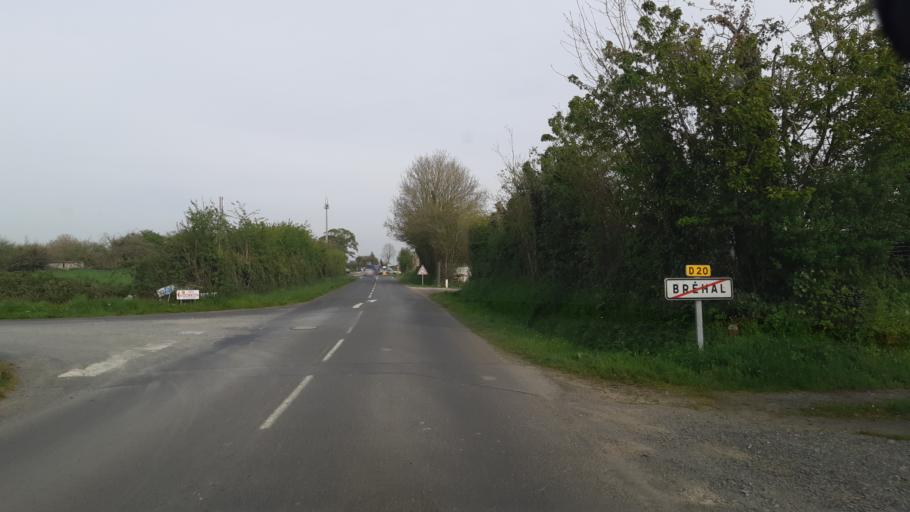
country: FR
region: Lower Normandy
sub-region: Departement de la Manche
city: Brehal
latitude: 48.8962
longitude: -1.5050
